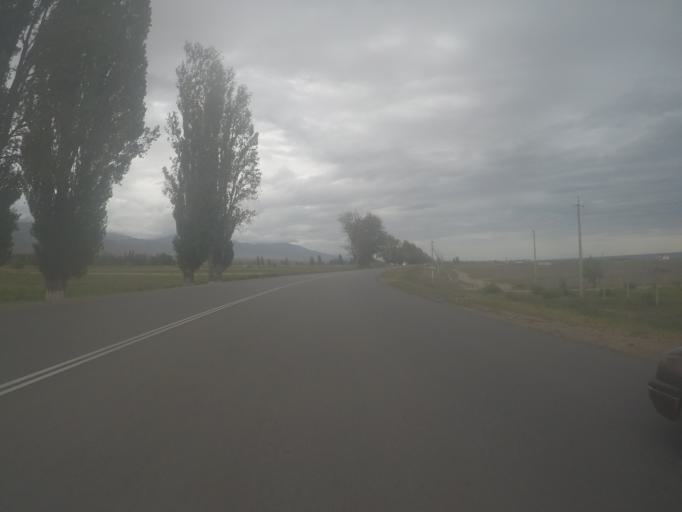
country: KG
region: Ysyk-Koel
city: Cholpon-Ata
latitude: 42.5932
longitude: 76.7561
